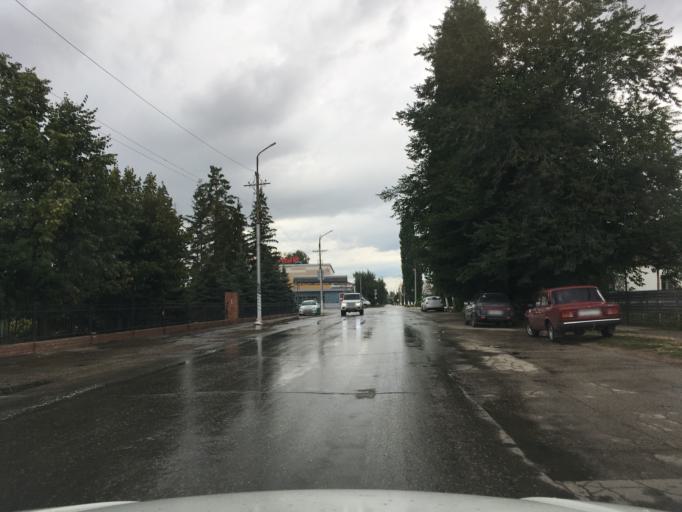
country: RU
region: Samara
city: Bezenchuk
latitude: 52.9845
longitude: 49.4399
